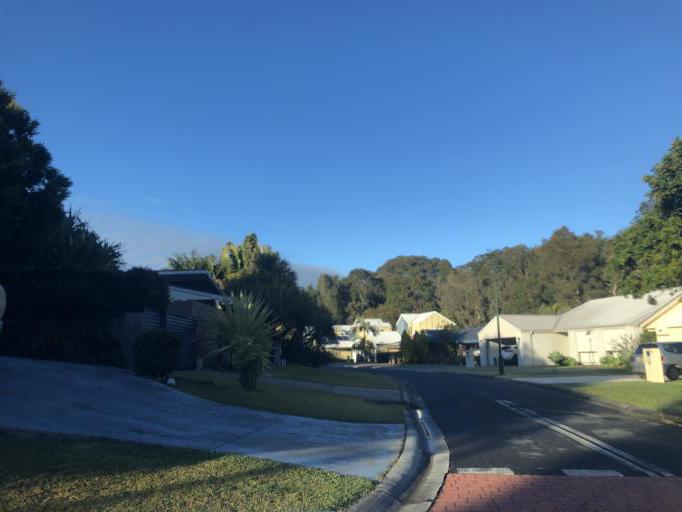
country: AU
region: New South Wales
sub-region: Coffs Harbour
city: Coffs Harbour
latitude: -30.2929
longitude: 153.1294
